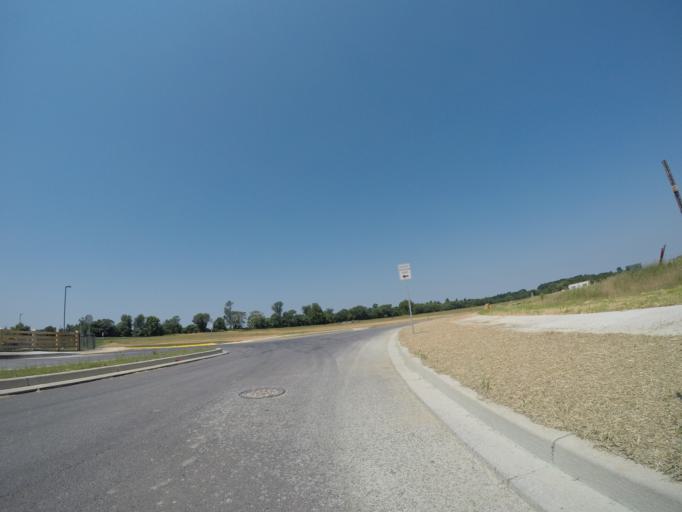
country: US
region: Maryland
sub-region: Frederick County
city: Urbana
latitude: 39.3280
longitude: -77.3659
